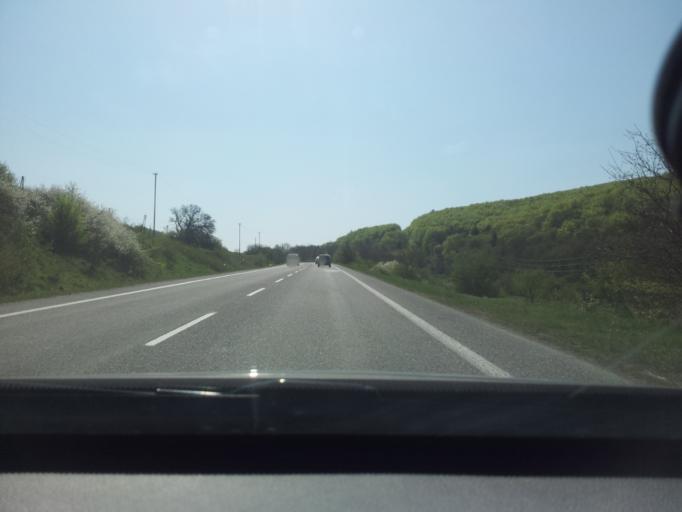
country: SK
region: Trenciansky
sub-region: Okres Trencin
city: Trencin
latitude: 48.8198
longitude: 18.0777
